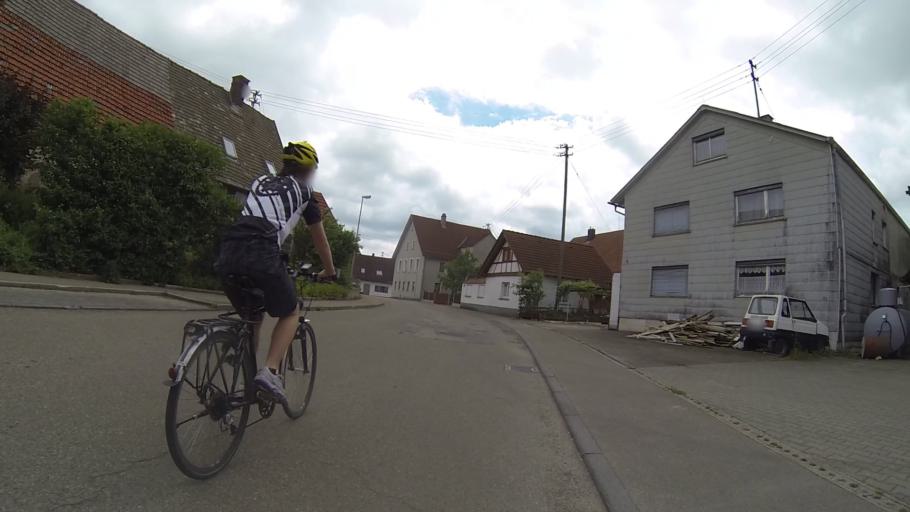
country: DE
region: Baden-Wuerttemberg
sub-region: Regierungsbezirk Stuttgart
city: Bohmenkirch
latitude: 48.6725
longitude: 9.9849
